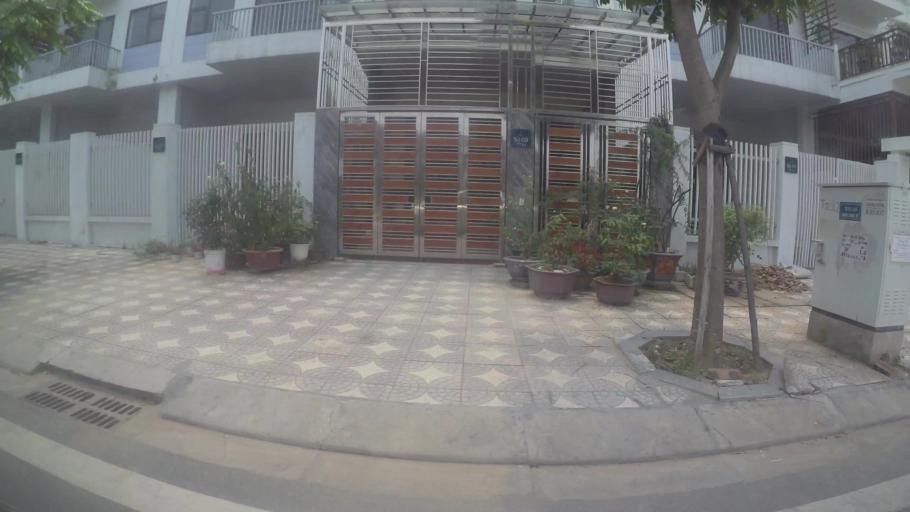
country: VN
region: Ha Noi
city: Cau Dien
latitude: 21.0256
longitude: 105.7429
